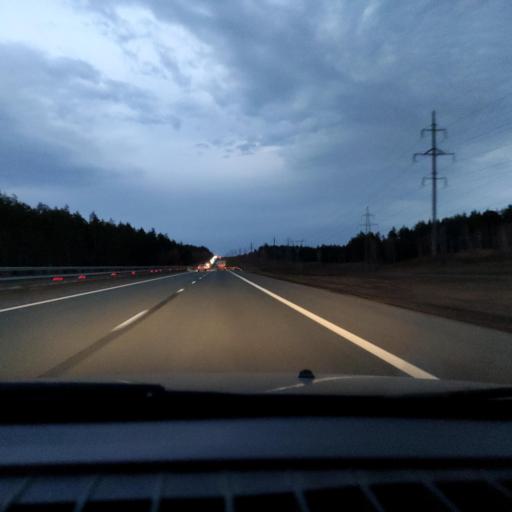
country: RU
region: Samara
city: Povolzhskiy
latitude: 53.5170
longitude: 49.7609
